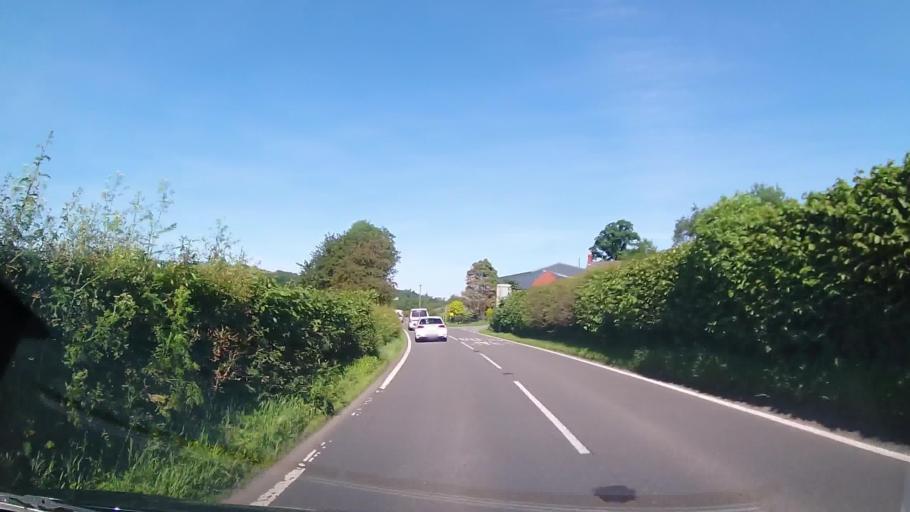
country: GB
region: Wales
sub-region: Sir Powys
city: Llanfyllin
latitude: 52.6642
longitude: -3.2942
